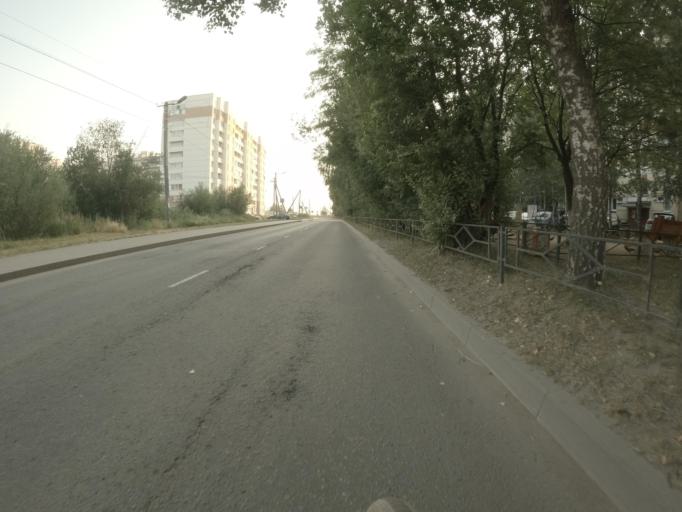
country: RU
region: St.-Petersburg
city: Pontonnyy
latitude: 59.7988
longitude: 30.6367
